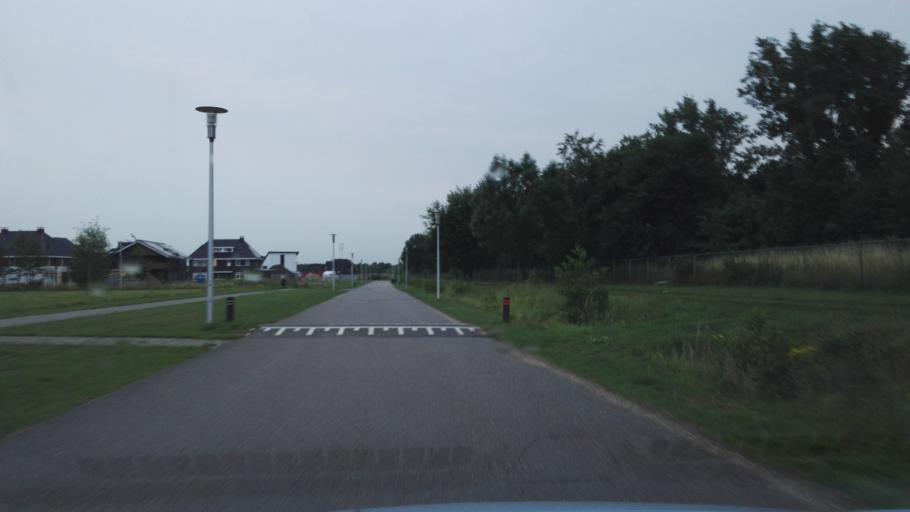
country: NL
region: Gelderland
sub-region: Gemeente Apeldoorn
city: Apeldoorn
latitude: 52.2036
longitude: 6.0058
